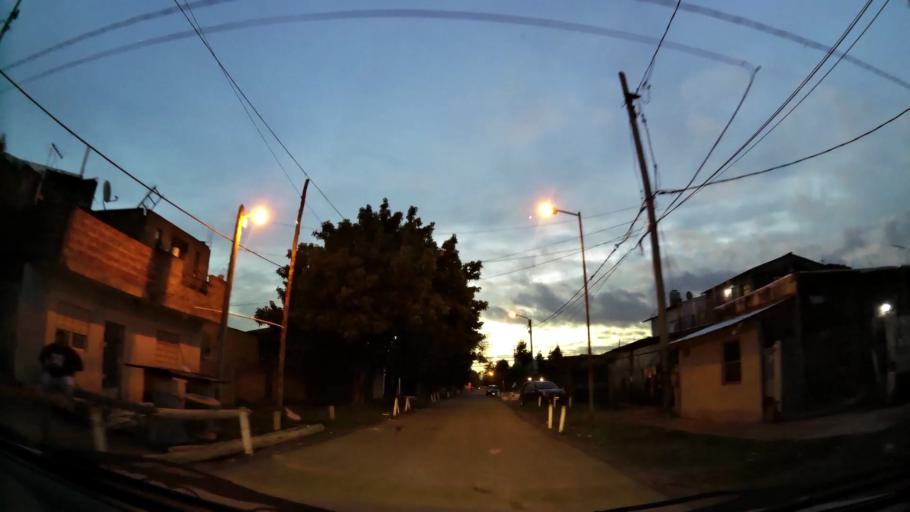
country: AR
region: Buenos Aires
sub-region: Partido de Lomas de Zamora
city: Lomas de Zamora
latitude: -34.7458
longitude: -58.3588
